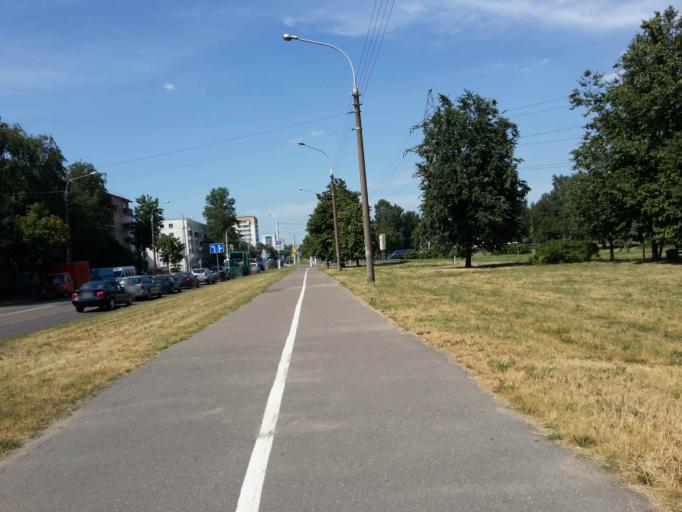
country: BY
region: Minsk
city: Minsk
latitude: 53.9308
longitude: 27.5661
